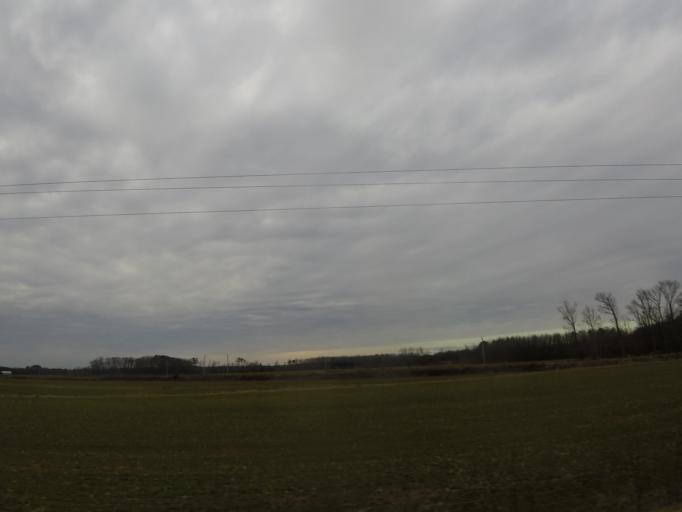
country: US
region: North Carolina
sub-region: Halifax County
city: Scotland Neck
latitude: 36.2371
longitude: -77.3526
